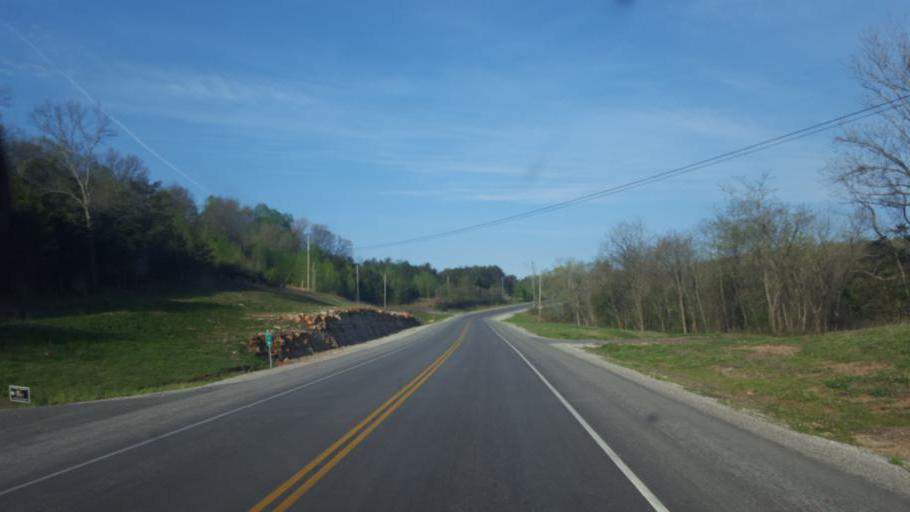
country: US
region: Kentucky
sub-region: Hart County
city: Munfordville
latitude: 37.2744
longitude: -85.9218
